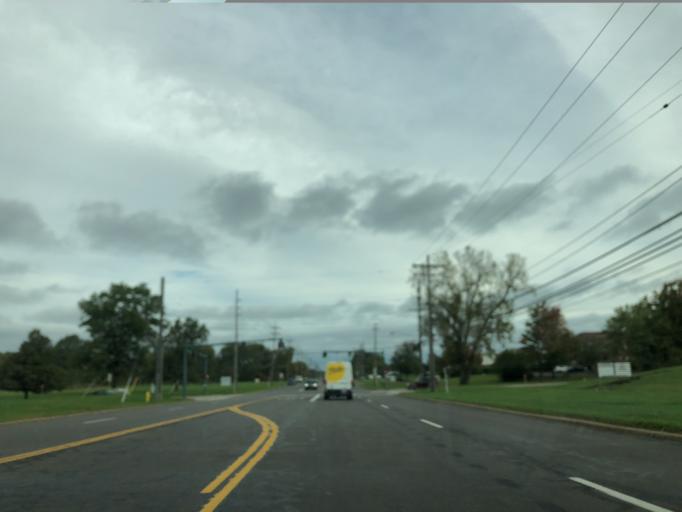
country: US
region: Ohio
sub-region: Cuyahoga County
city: Brecksville
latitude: 41.2822
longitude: -81.6272
